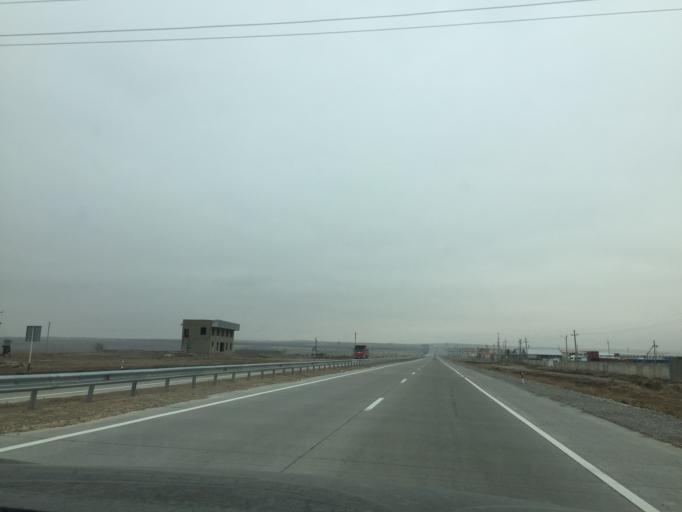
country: KZ
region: Ongtustik Qazaqstan
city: Aksu
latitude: 42.4745
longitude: 69.8206
